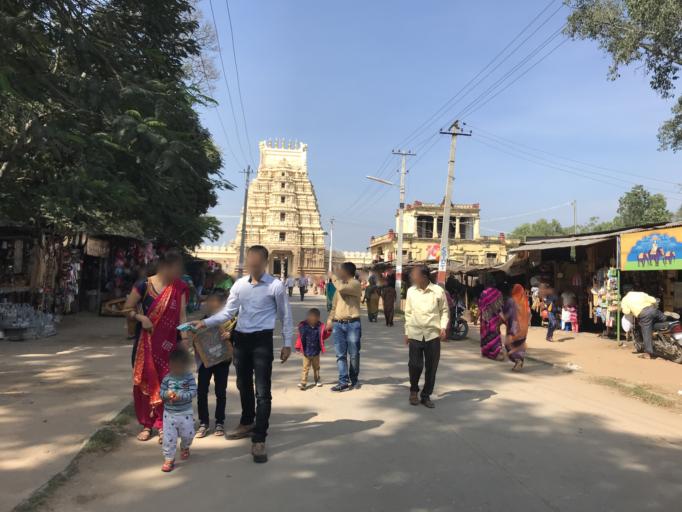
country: IN
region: Karnataka
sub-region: Mandya
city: Shrirangapattana
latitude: 12.4249
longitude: 76.6808
